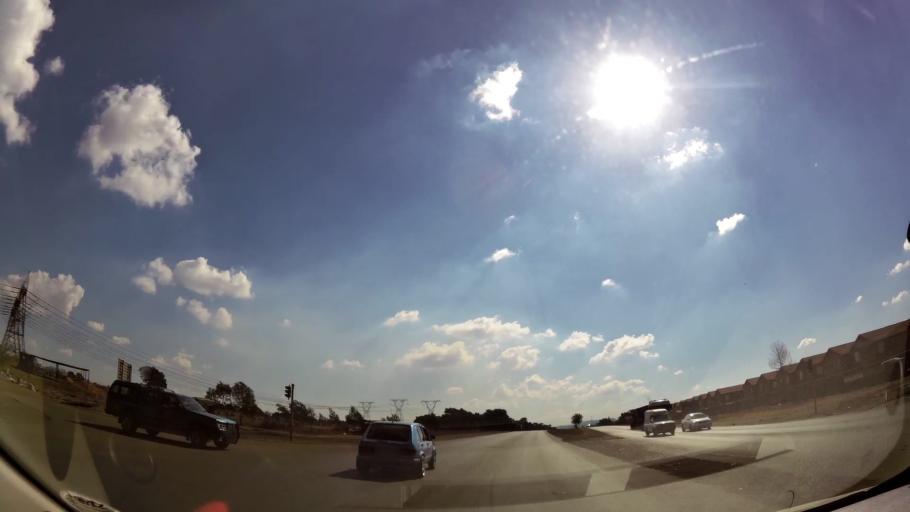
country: ZA
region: Mpumalanga
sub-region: Nkangala District Municipality
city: Witbank
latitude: -25.9514
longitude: 29.2487
